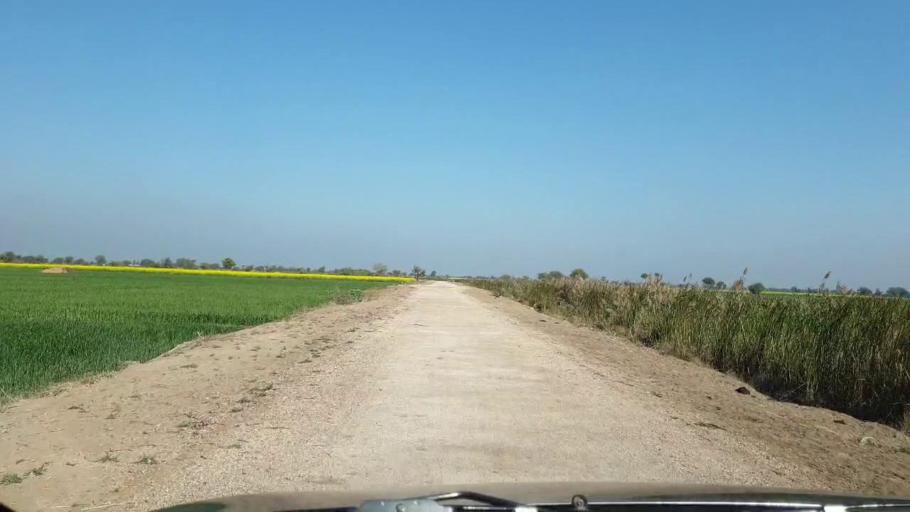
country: PK
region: Sindh
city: Sinjhoro
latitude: 25.9684
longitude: 68.7526
